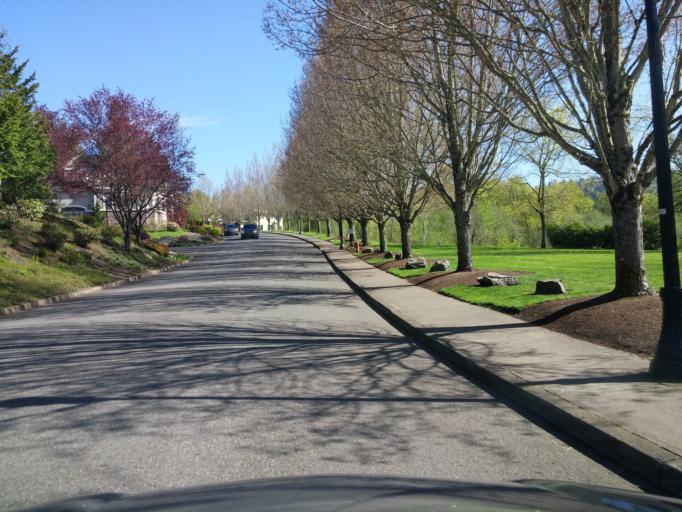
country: US
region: Oregon
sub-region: Washington County
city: West Haven
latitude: 45.5365
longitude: -122.7840
